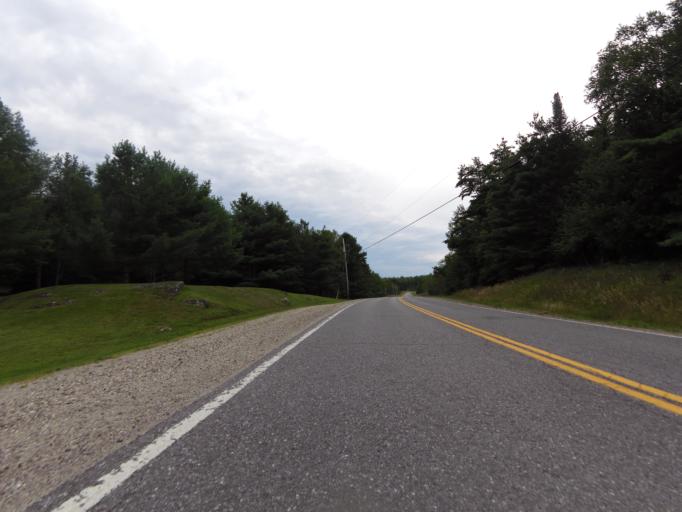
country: CA
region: Ontario
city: Carleton Place
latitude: 45.1138
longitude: -76.3583
